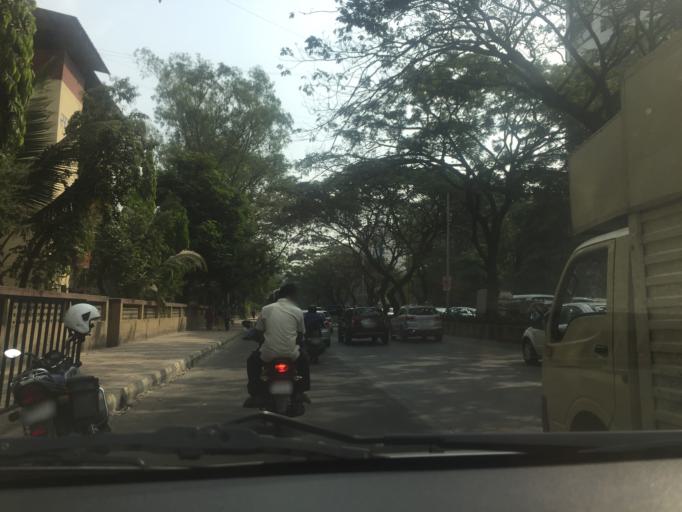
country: IN
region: Maharashtra
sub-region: Thane
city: Airoli
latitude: 19.1483
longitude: 72.9954
